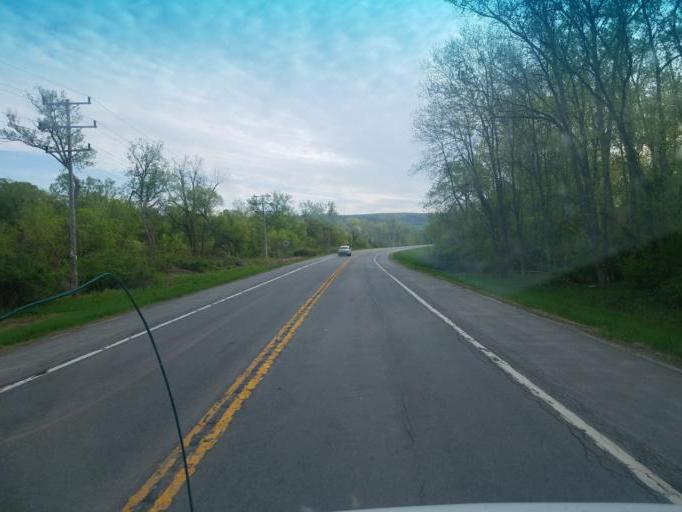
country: US
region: New York
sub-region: Herkimer County
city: Little Falls
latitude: 43.0283
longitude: -74.8709
